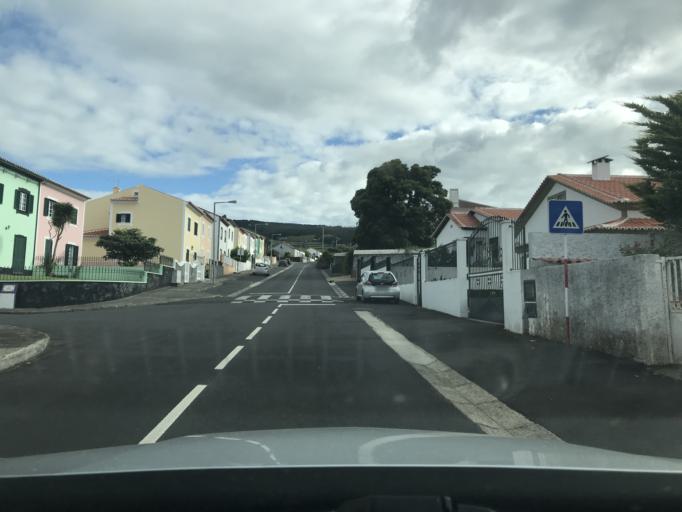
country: PT
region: Azores
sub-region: Angra do Heroismo
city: Angra do Heroismo
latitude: 38.6689
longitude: -27.2516
